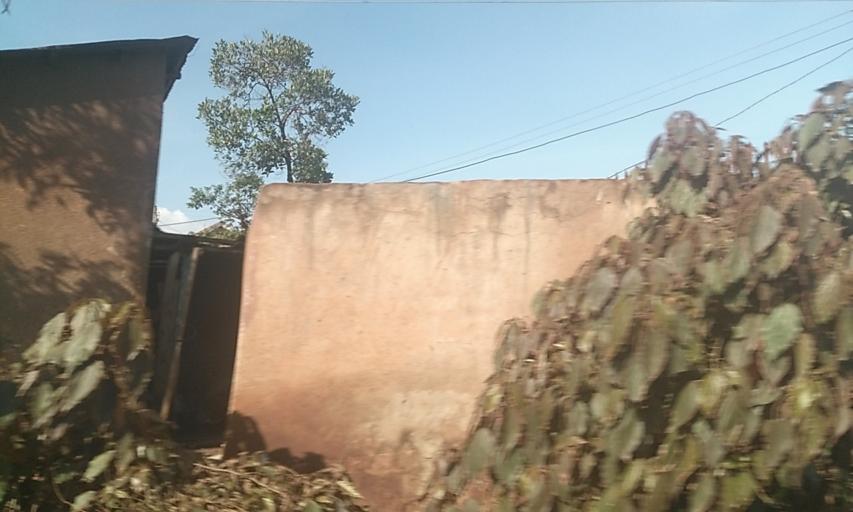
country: UG
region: Central Region
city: Kampala Central Division
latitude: 0.3236
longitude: 32.5415
